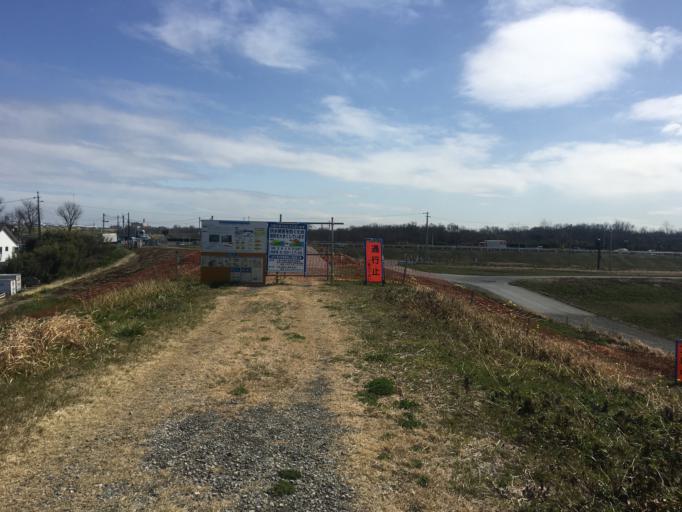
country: JP
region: Saitama
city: Shiki
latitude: 35.8609
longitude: 139.5951
